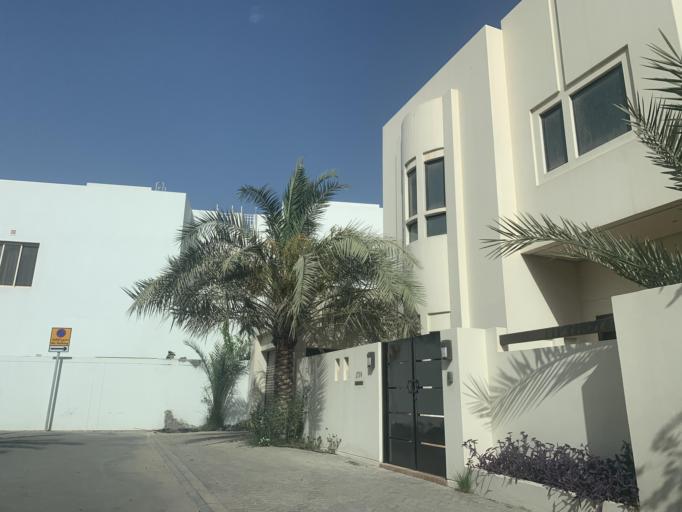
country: BH
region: Northern
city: Madinat `Isa
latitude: 26.1652
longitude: 50.5749
